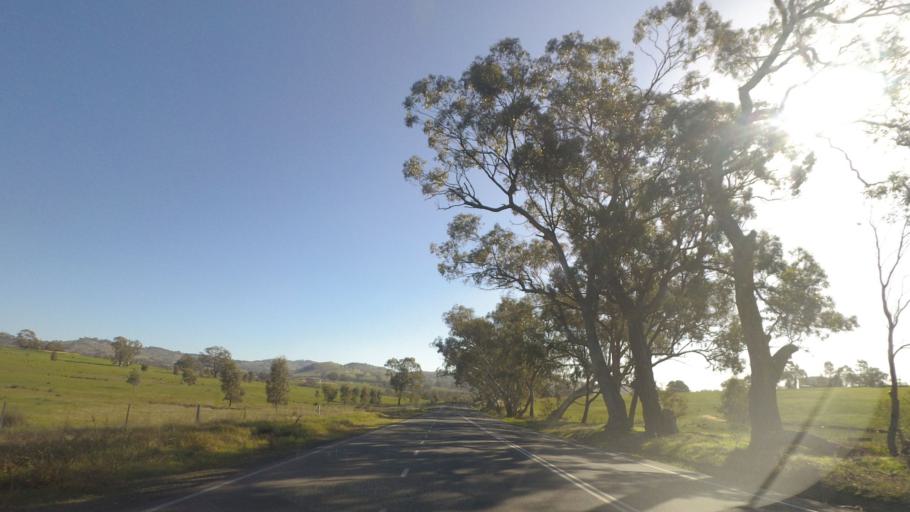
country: AU
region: Victoria
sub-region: Mount Alexander
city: Castlemaine
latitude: -36.9532
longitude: 144.3431
